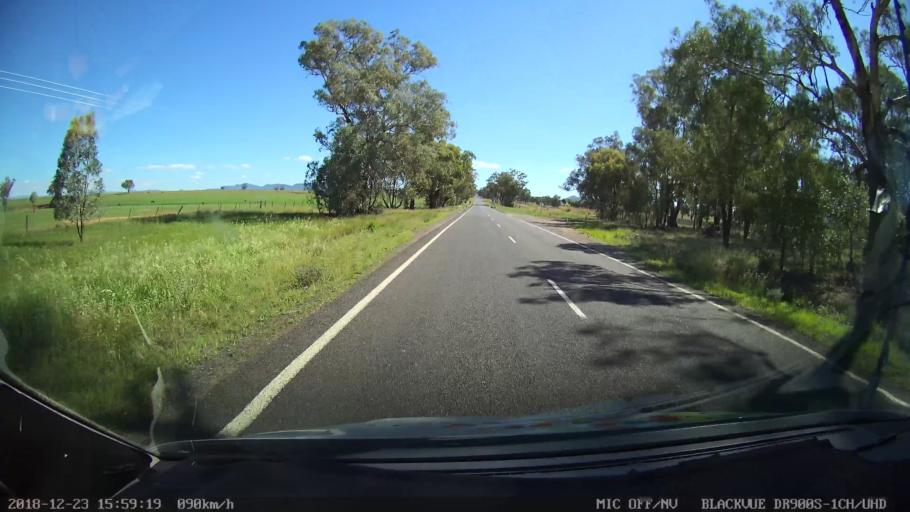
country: AU
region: New South Wales
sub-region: Tamworth Municipality
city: Phillip
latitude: -31.1983
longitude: 150.8343
